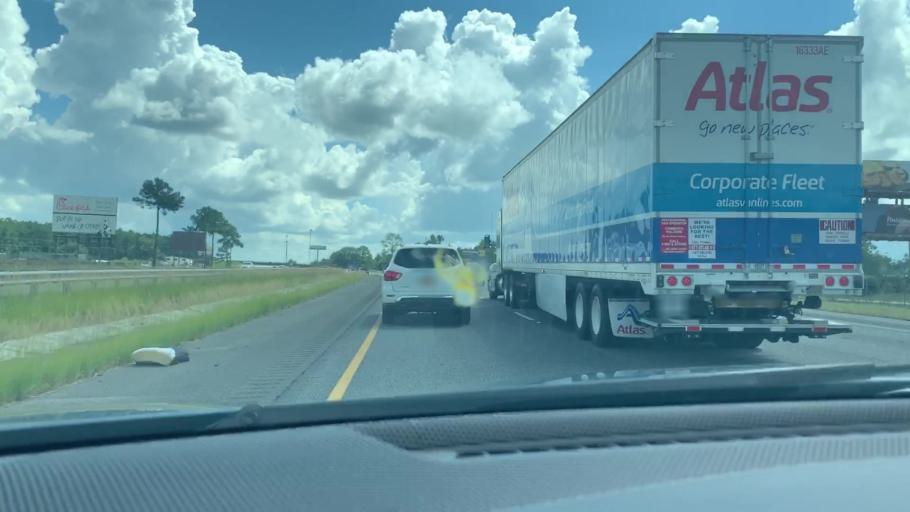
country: US
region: Georgia
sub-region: Lowndes County
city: Valdosta
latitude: 30.6980
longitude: -83.2438
